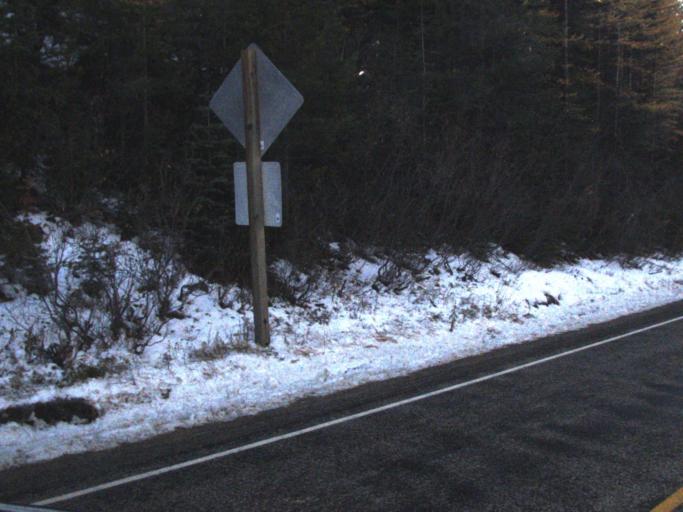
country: US
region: Washington
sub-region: Ferry County
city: Republic
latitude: 48.6064
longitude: -118.4594
